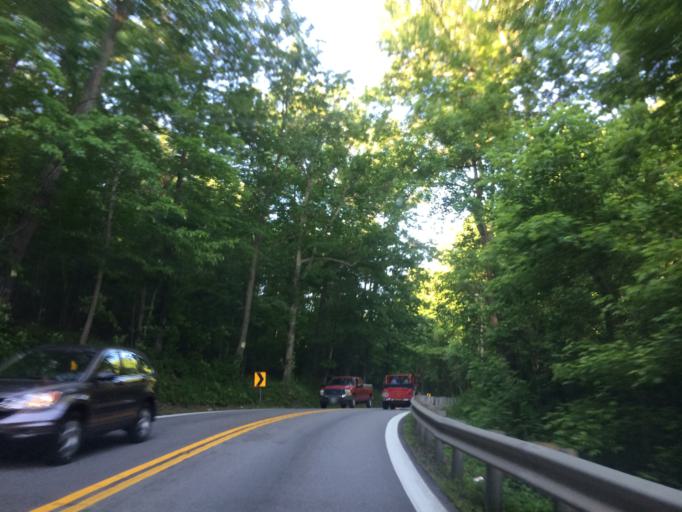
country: US
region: Maryland
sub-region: Carroll County
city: Sykesville
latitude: 39.3521
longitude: -77.0159
